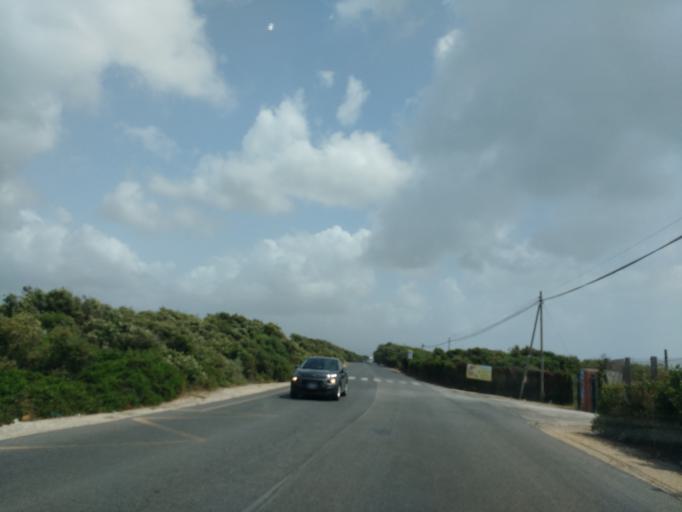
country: IT
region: Latium
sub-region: Citta metropolitana di Roma Capitale
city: Torvaianica
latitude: 41.6781
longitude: 12.3873
